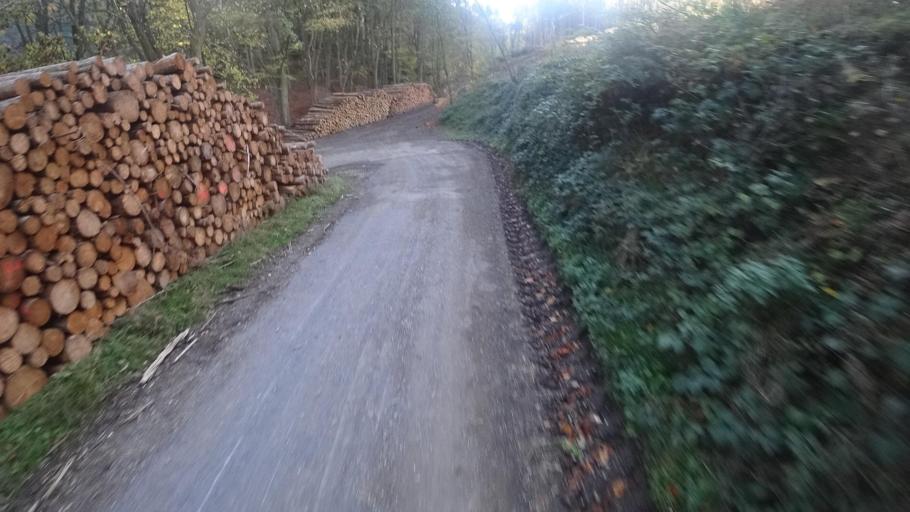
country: DE
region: Rheinland-Pfalz
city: Lind
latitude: 50.5016
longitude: 6.9148
